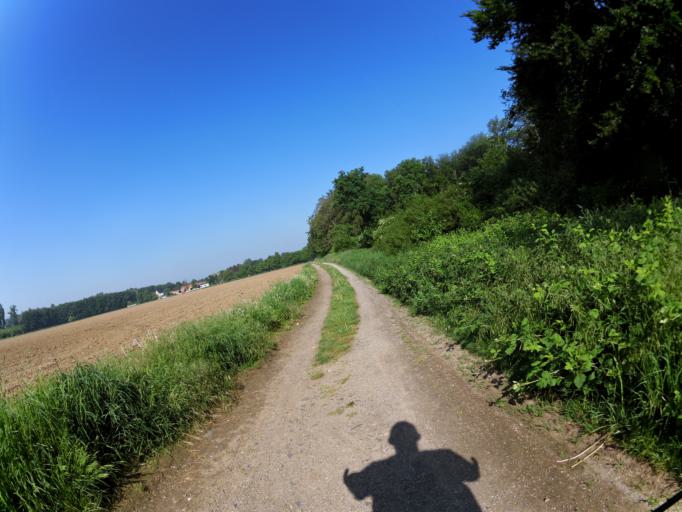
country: DE
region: North Rhine-Westphalia
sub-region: Regierungsbezirk Koln
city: Linnich
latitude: 50.9571
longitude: 6.3139
